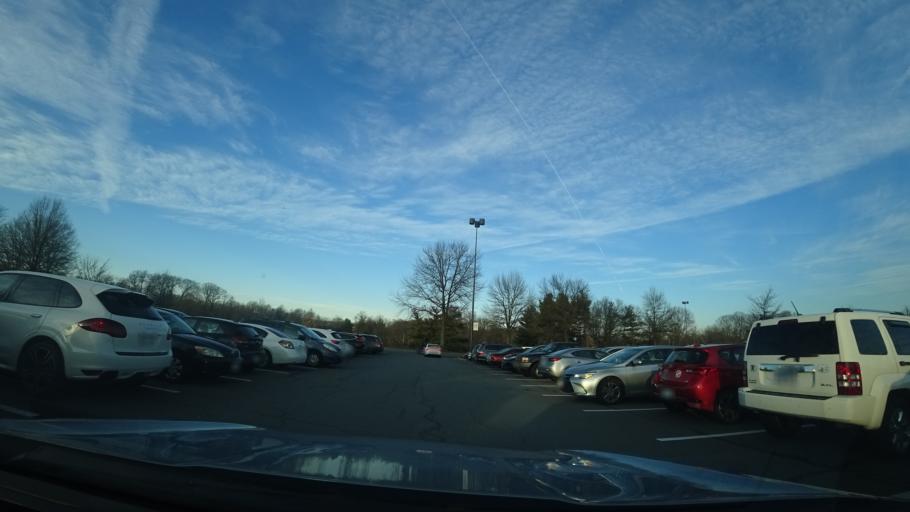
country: US
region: Virginia
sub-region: Fairfax County
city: Greenbriar
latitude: 38.8644
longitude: -77.3581
